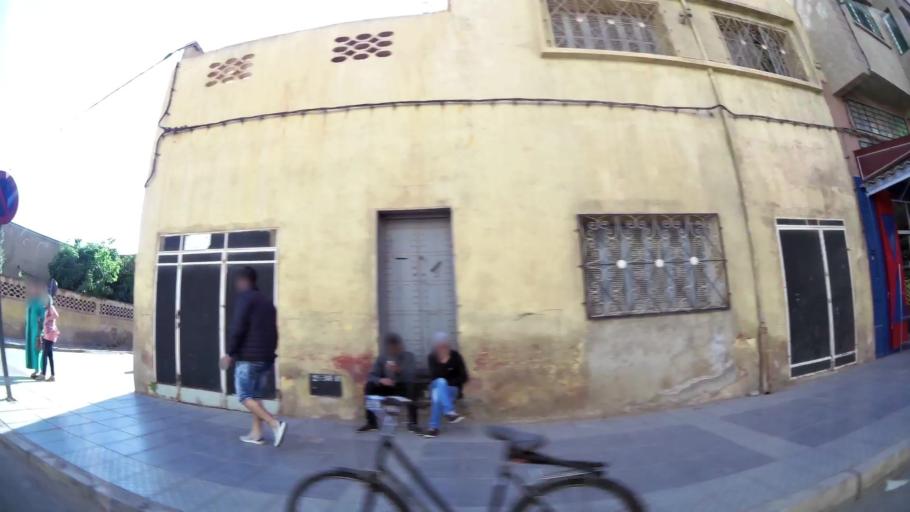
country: MA
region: Oriental
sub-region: Oujda-Angad
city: Oujda
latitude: 34.6763
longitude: -1.9089
